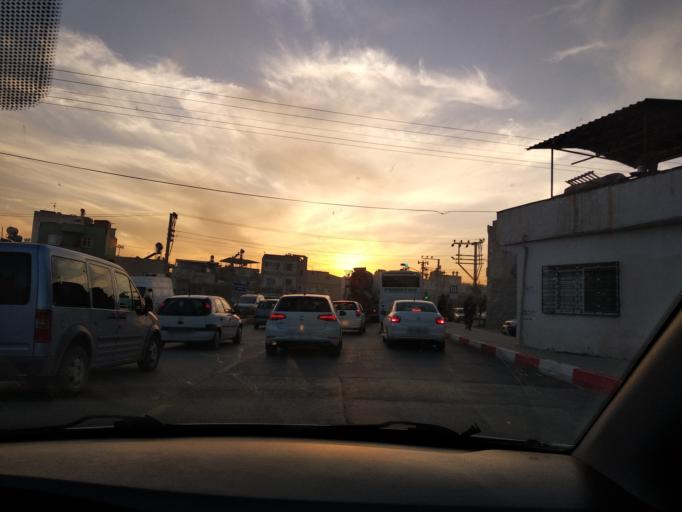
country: TR
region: Mersin
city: Mercin
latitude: 36.8268
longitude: 34.6065
